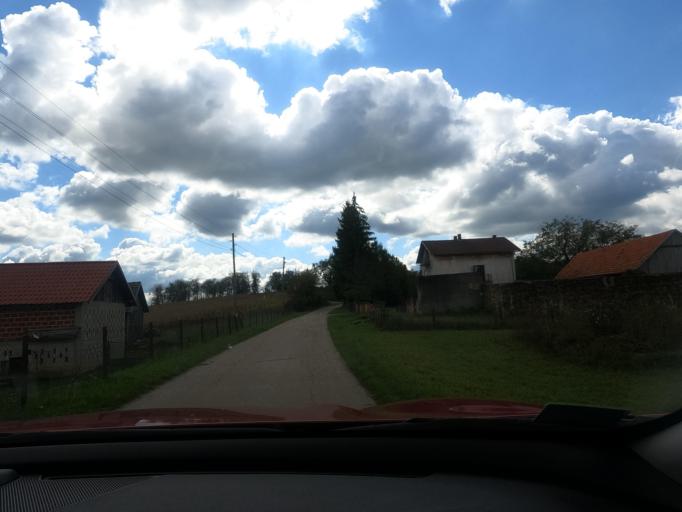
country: HR
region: Karlovacka
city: Vojnic
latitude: 45.2438
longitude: 15.7118
